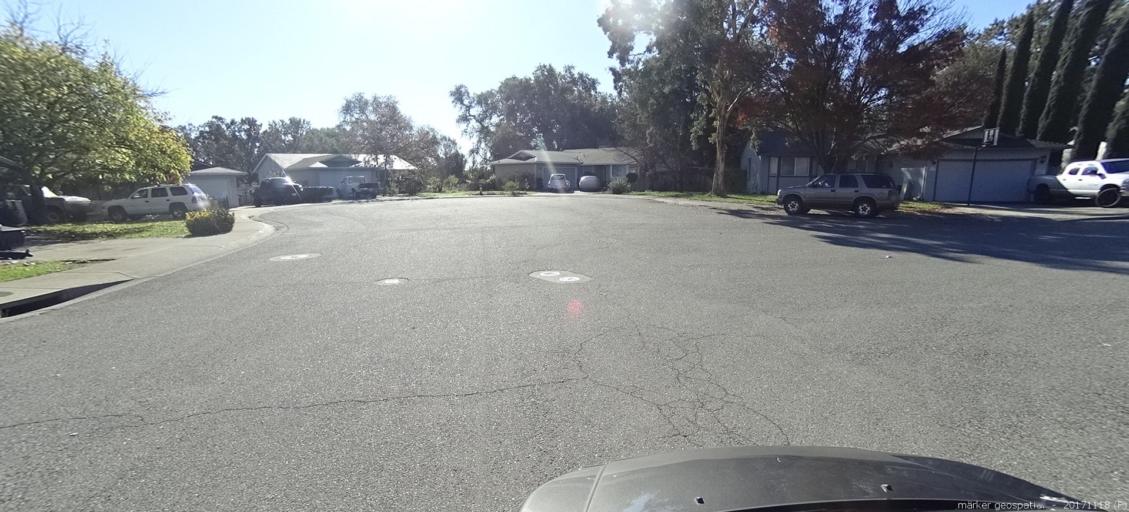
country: US
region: California
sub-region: Shasta County
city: Cottonwood
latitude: 40.3839
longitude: -122.2885
